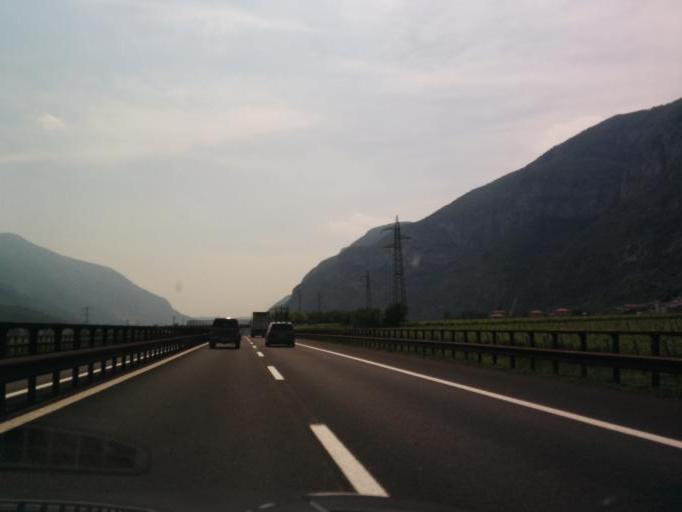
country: IT
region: Veneto
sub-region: Provincia di Verona
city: Dolce
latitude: 45.6275
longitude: 10.8667
